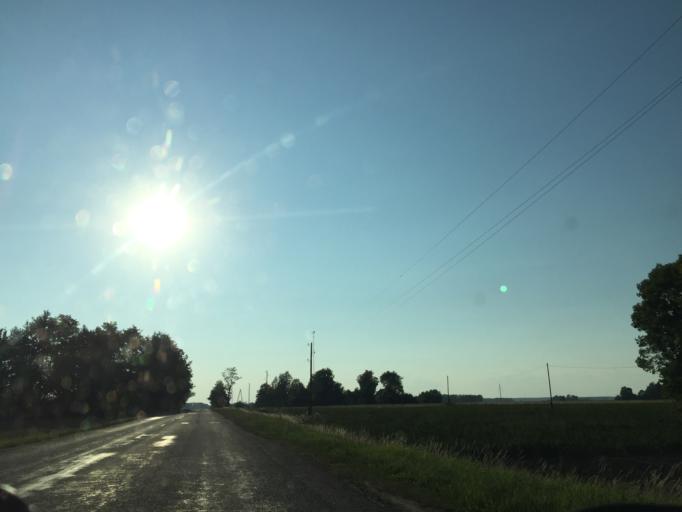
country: LV
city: Tervete
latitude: 56.4366
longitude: 23.5137
